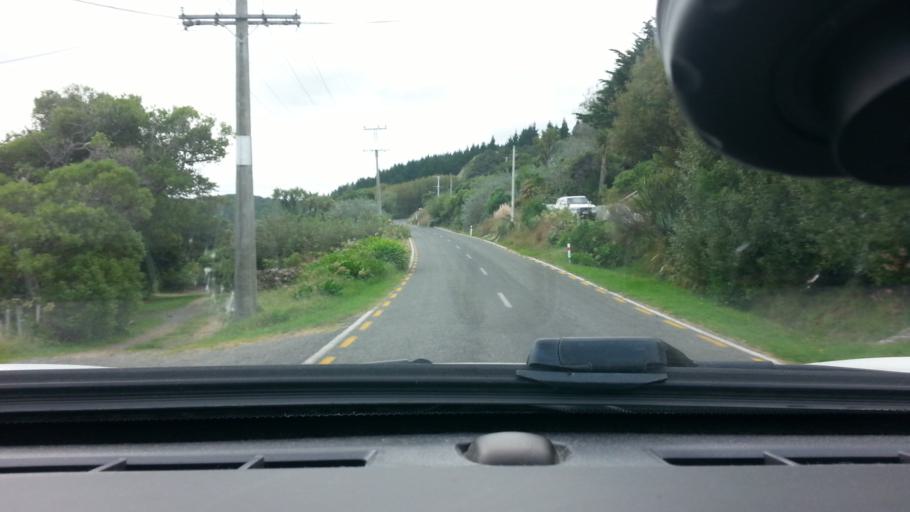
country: NZ
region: Wellington
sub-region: South Wairarapa District
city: Waipawa
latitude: -41.4582
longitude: 175.2200
